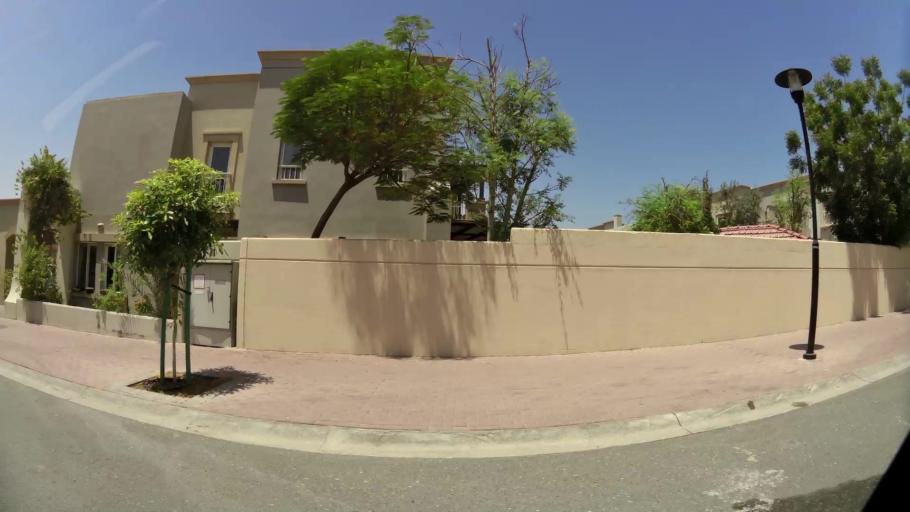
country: AE
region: Dubai
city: Dubai
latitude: 25.0544
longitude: 55.1742
